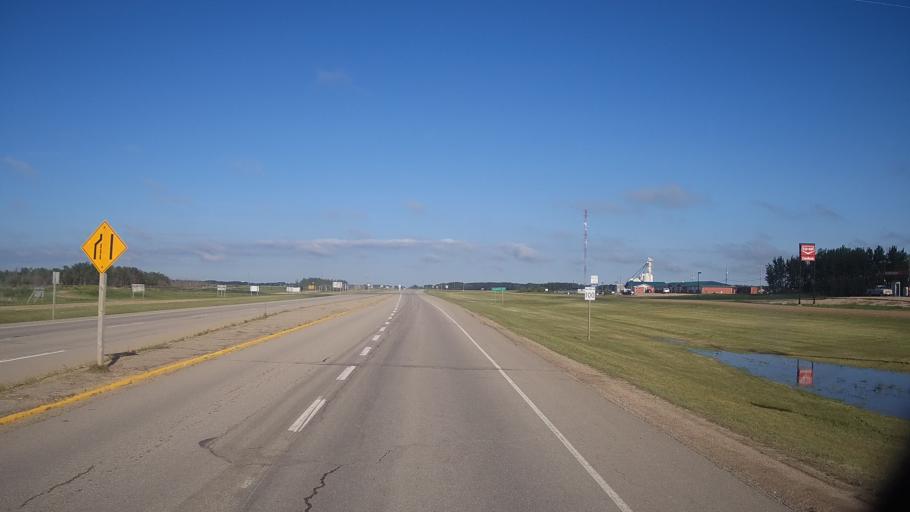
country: CA
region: Saskatchewan
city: Lanigan
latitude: 51.8477
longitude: -105.0437
